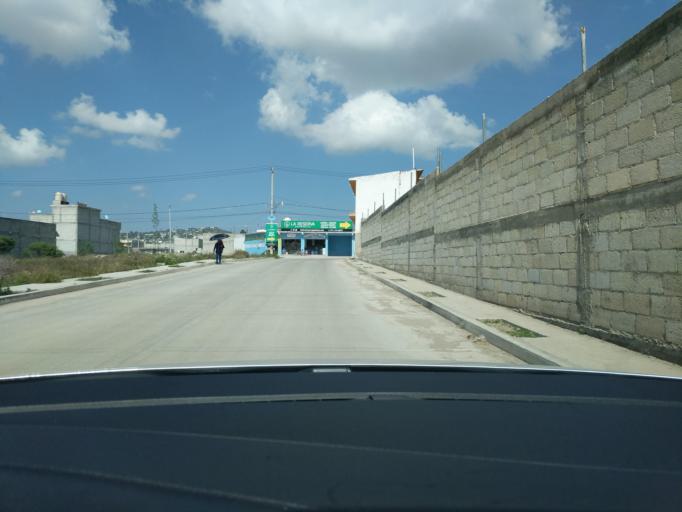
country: MX
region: Hidalgo
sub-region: Zempoala
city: El Mirador
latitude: 20.0244
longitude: -98.8127
